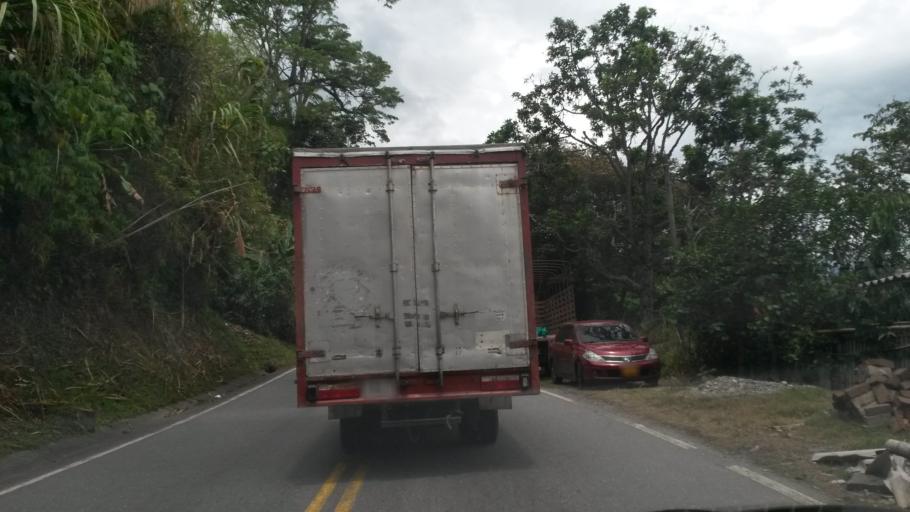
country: CO
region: Cauca
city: Rosas
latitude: 2.2603
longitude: -76.7512
